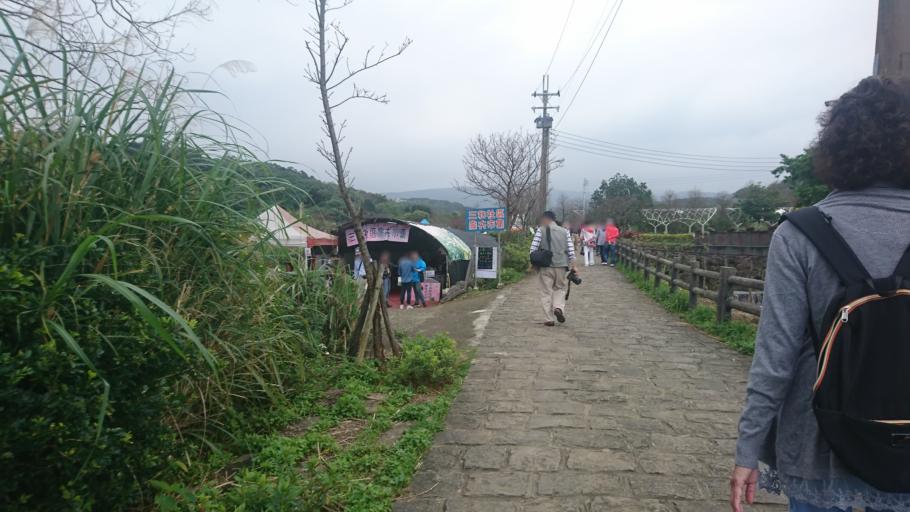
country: TW
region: Taipei
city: Taipei
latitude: 25.2681
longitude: 121.5105
